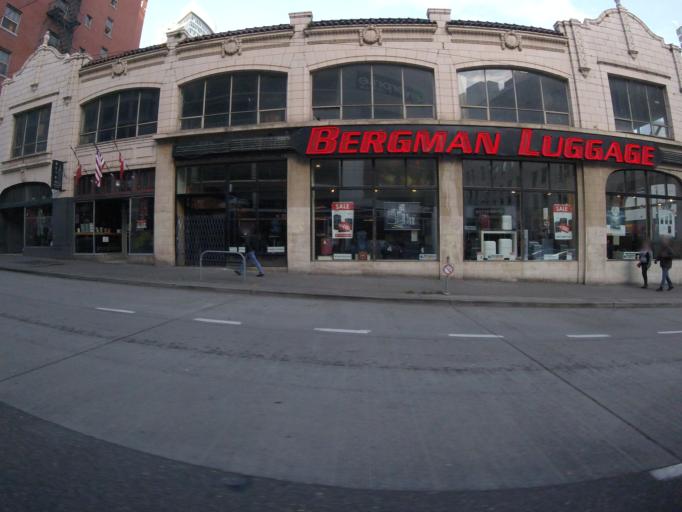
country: US
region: Washington
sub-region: King County
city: Seattle
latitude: 47.6114
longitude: -122.3398
